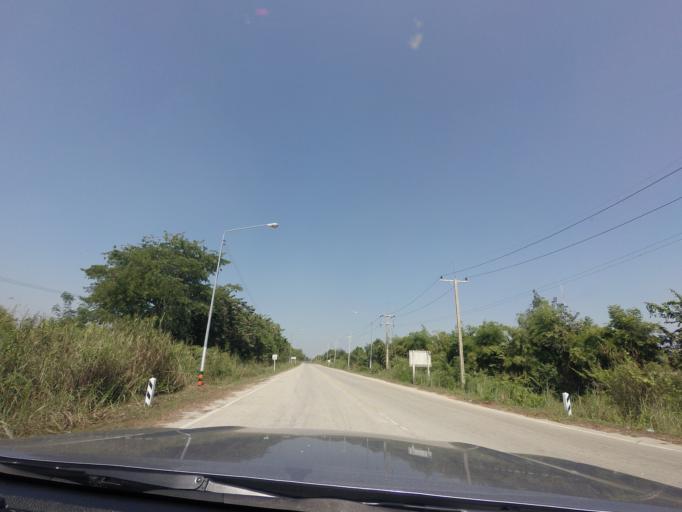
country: TH
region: Sukhothai
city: Sukhothai
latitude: 17.0686
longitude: 99.7923
